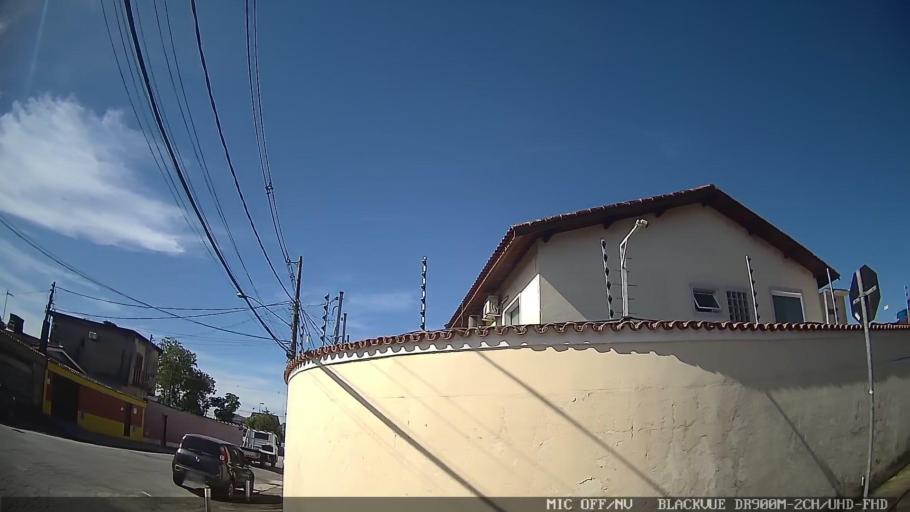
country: BR
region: Sao Paulo
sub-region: Santos
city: Santos
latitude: -23.9417
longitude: -46.2834
